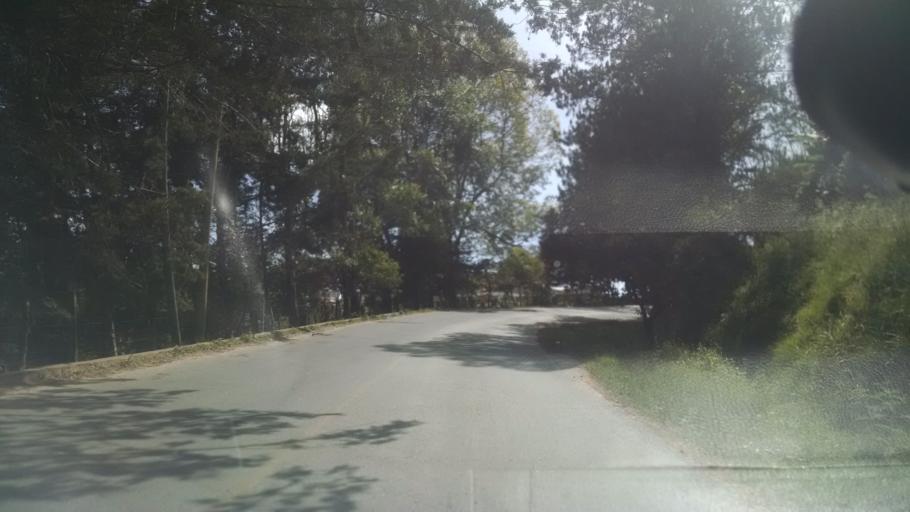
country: CO
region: Antioquia
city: Guatape
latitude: 6.2226
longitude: -75.2474
